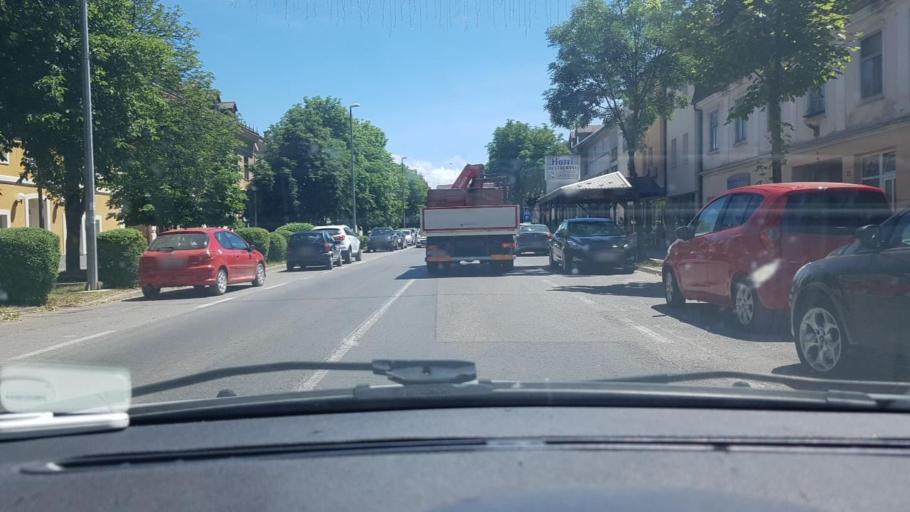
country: HR
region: Licko-Senjska
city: Otocac
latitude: 44.8696
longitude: 15.2388
